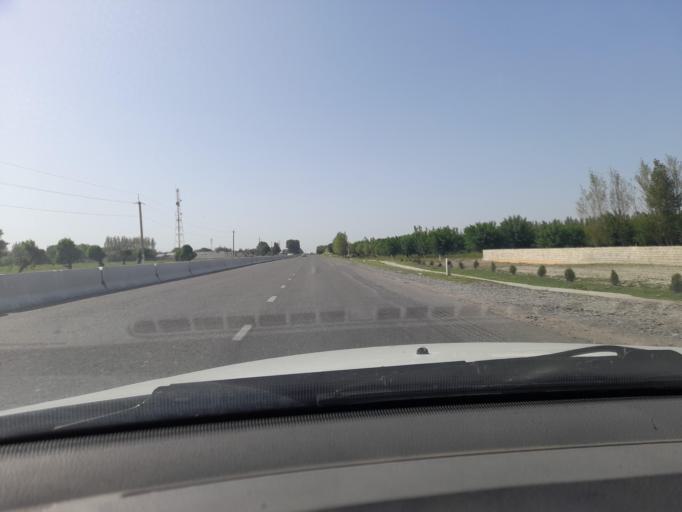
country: UZ
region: Samarqand
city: Daxbet
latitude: 39.8109
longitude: 66.8552
